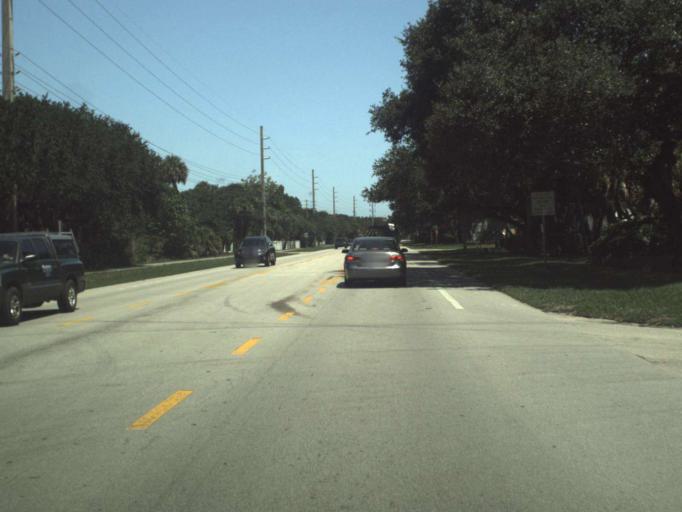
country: US
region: Florida
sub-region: Indian River County
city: South Beach
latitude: 27.6276
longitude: -80.3547
